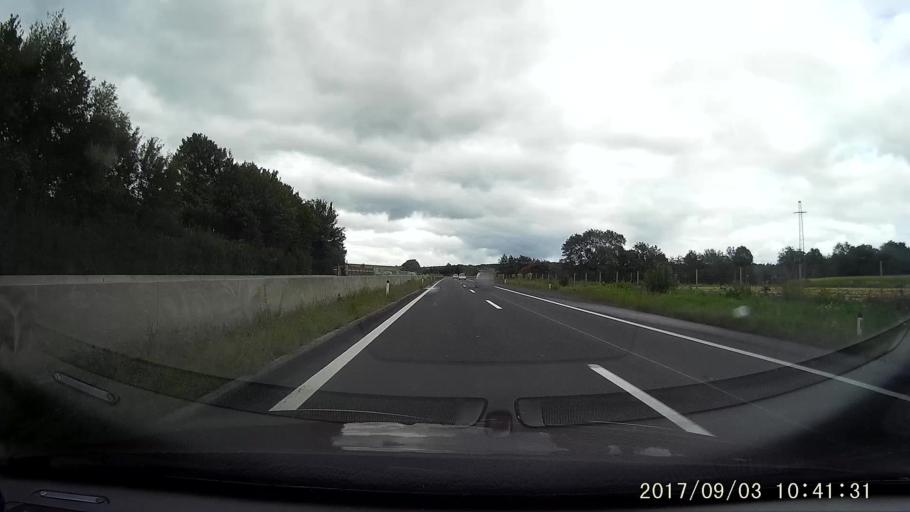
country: AT
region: Styria
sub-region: Politischer Bezirk Hartberg-Fuerstenfeld
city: Sankt Johann in der Haide
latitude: 47.2473
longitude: 15.9985
